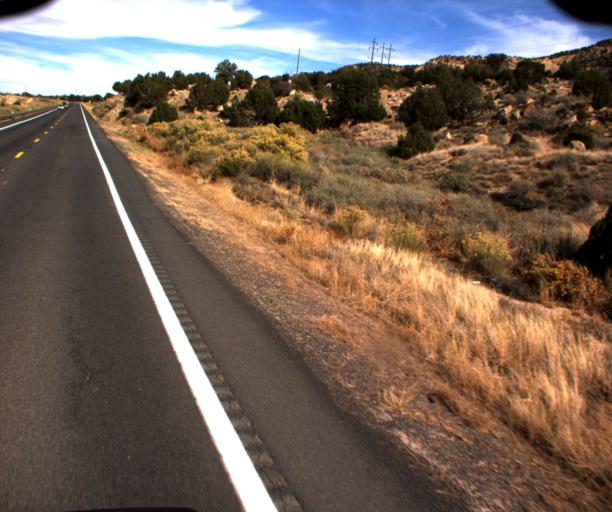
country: US
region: Arizona
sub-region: Navajo County
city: Kayenta
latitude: 36.6367
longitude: -110.4437
